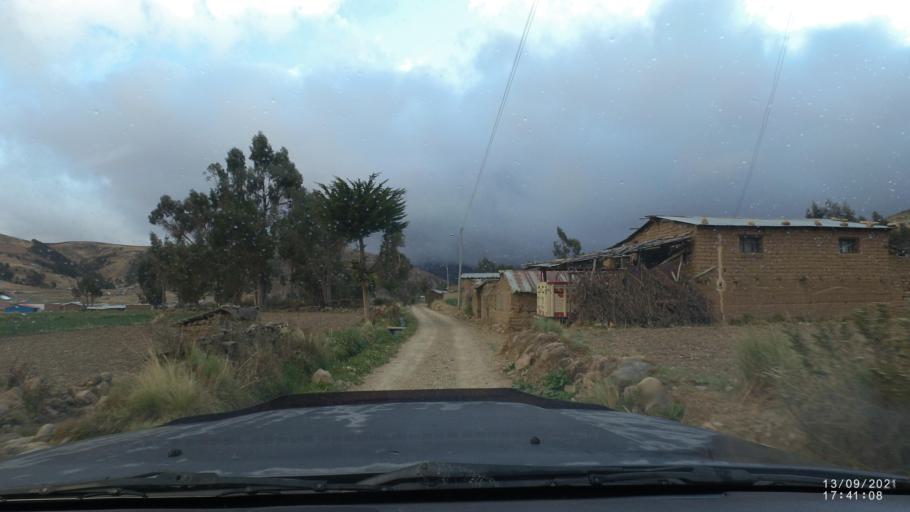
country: BO
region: Cochabamba
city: Colomi
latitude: -17.3641
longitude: -65.8115
